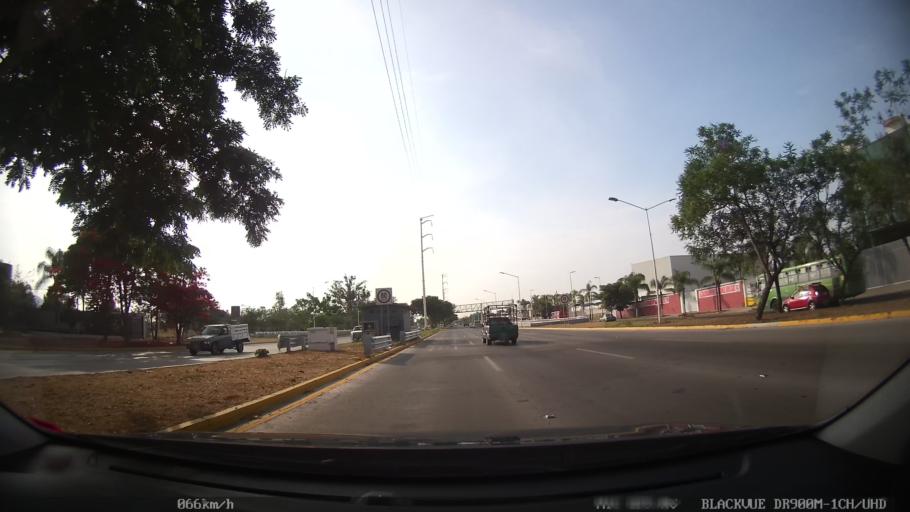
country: MX
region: Jalisco
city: Tlaquepaque
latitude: 20.7163
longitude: -103.3076
